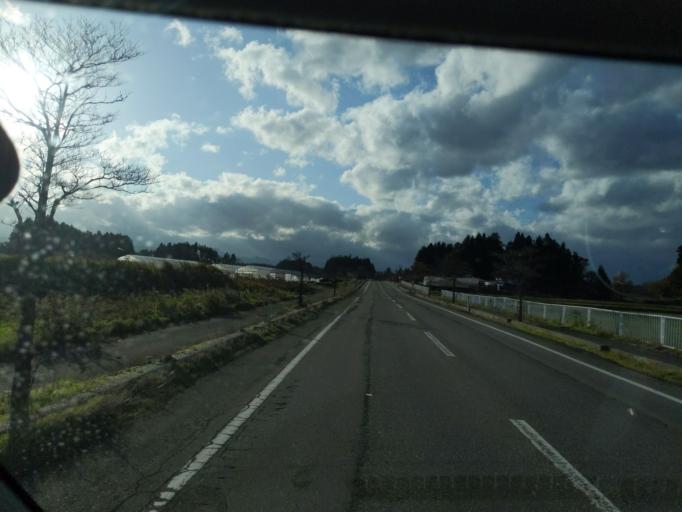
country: JP
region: Iwate
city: Mizusawa
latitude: 39.1127
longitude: 141.0633
